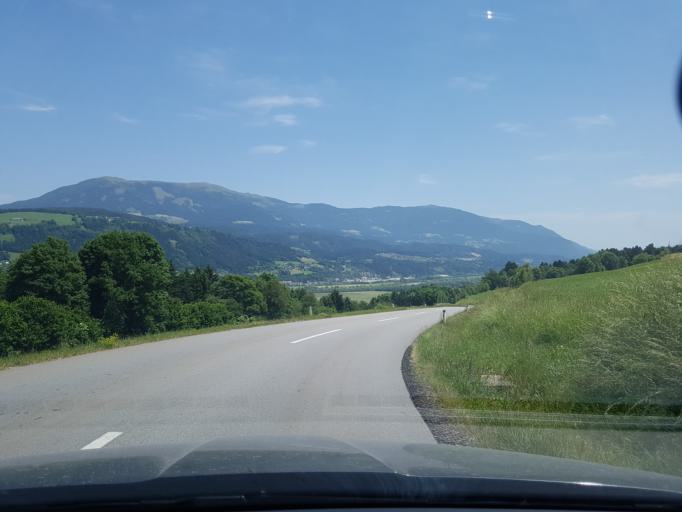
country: AT
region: Carinthia
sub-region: Politischer Bezirk Villach Land
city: Ferndorf
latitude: 46.7409
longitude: 13.5813
